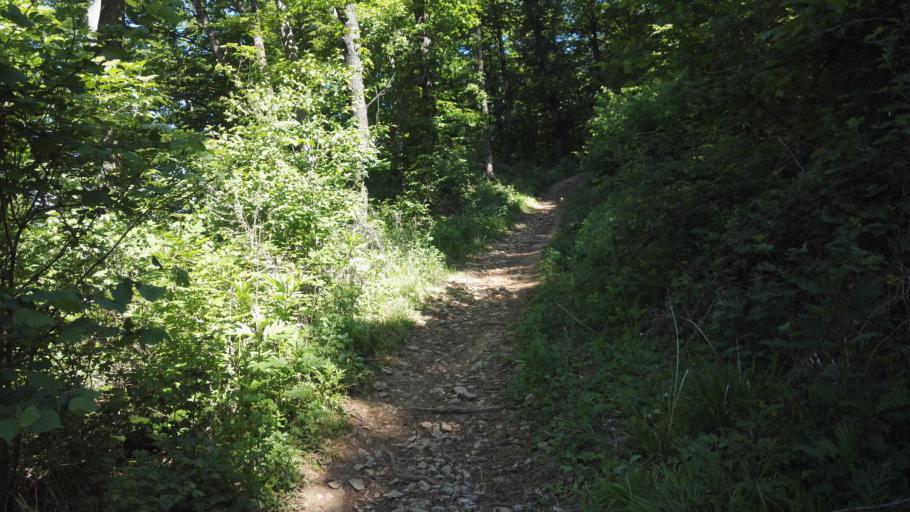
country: AT
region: Styria
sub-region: Politischer Bezirk Graz-Umgebung
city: Thal
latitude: 47.0757
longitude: 15.3690
